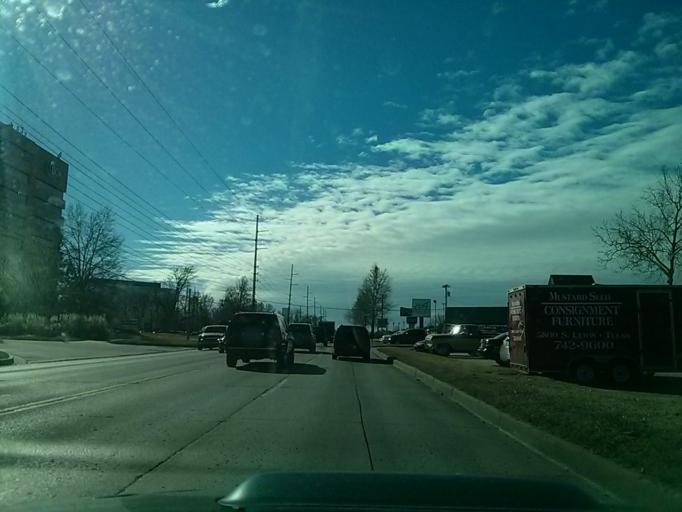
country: US
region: Oklahoma
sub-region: Tulsa County
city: Jenks
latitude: 36.0802
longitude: -95.9581
